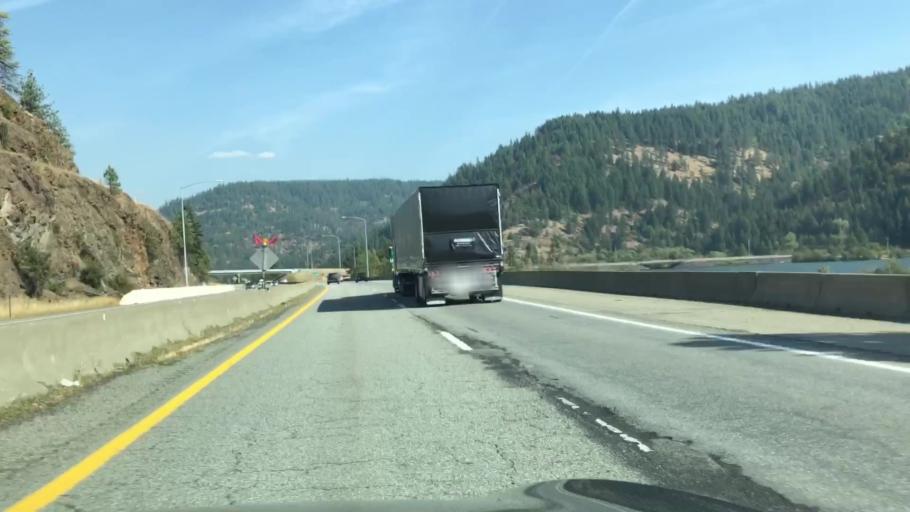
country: US
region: Idaho
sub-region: Kootenai County
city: Coeur d'Alene
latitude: 47.6236
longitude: -116.6556
